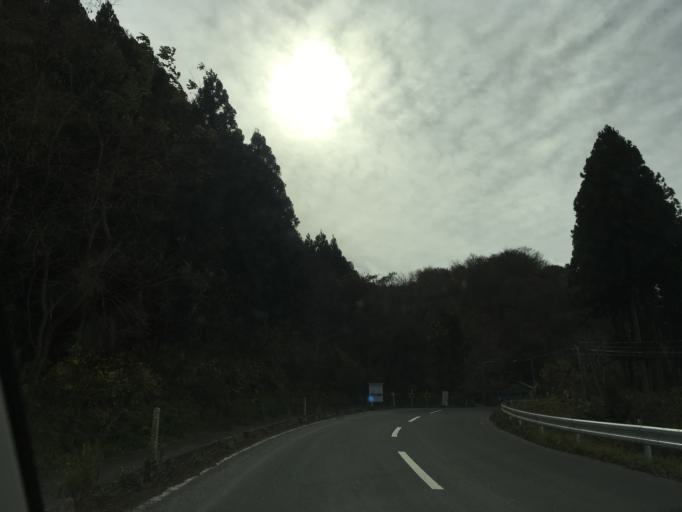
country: JP
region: Iwate
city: Ichinoseki
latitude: 38.7510
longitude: 141.2858
